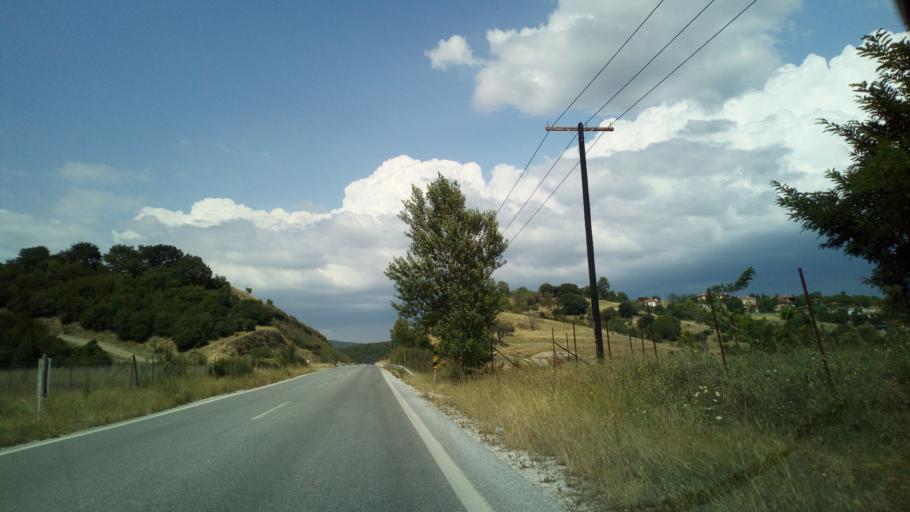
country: GR
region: Central Macedonia
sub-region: Nomos Chalkidikis
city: Polygyros
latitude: 40.4346
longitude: 23.4178
